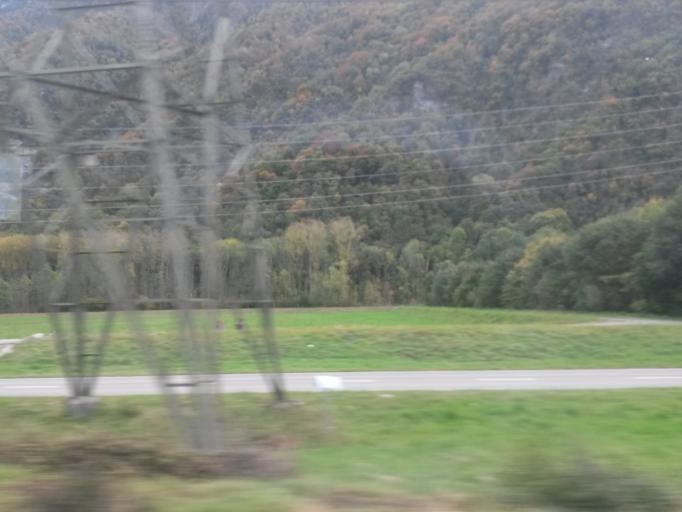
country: CH
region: Vaud
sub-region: Aigle District
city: Villeneuve
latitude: 46.3756
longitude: 6.9266
